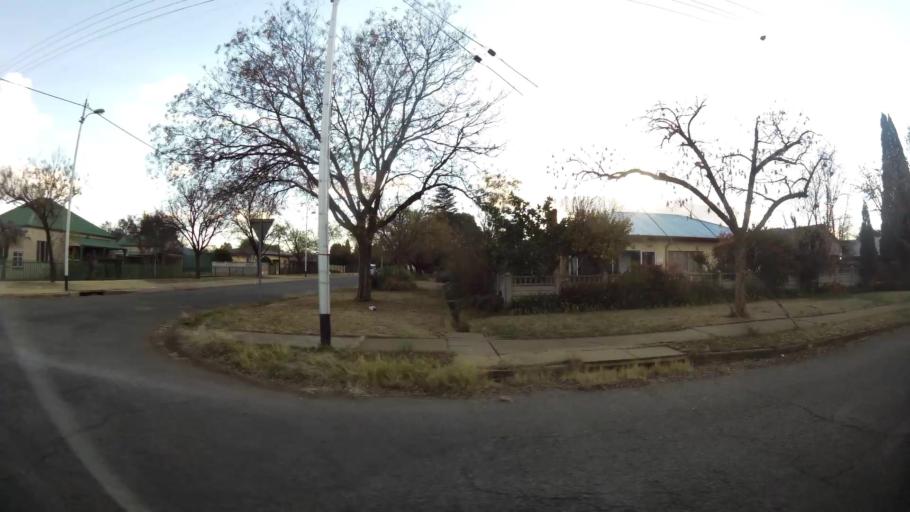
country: ZA
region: North-West
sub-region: Dr Kenneth Kaunda District Municipality
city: Potchefstroom
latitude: -26.7374
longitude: 27.0907
